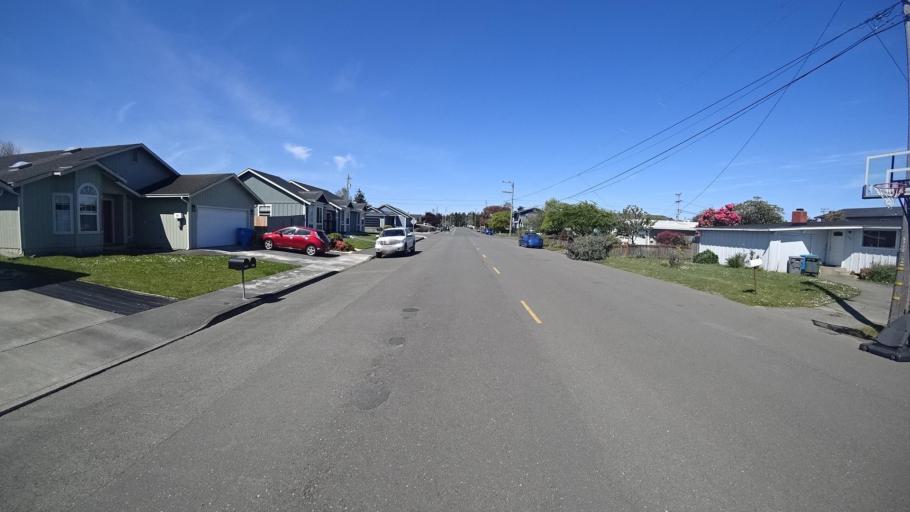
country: US
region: California
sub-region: Humboldt County
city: Myrtletown
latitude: 40.7878
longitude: -124.1254
